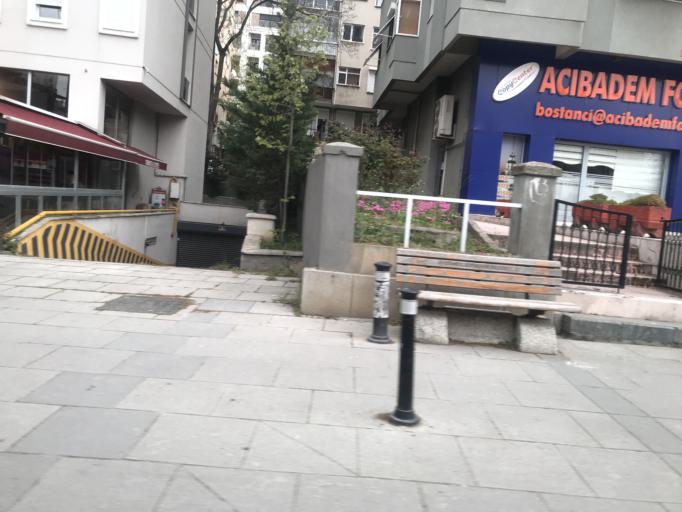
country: TR
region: Istanbul
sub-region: Atasehir
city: Atasehir
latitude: 40.9611
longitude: 29.0933
